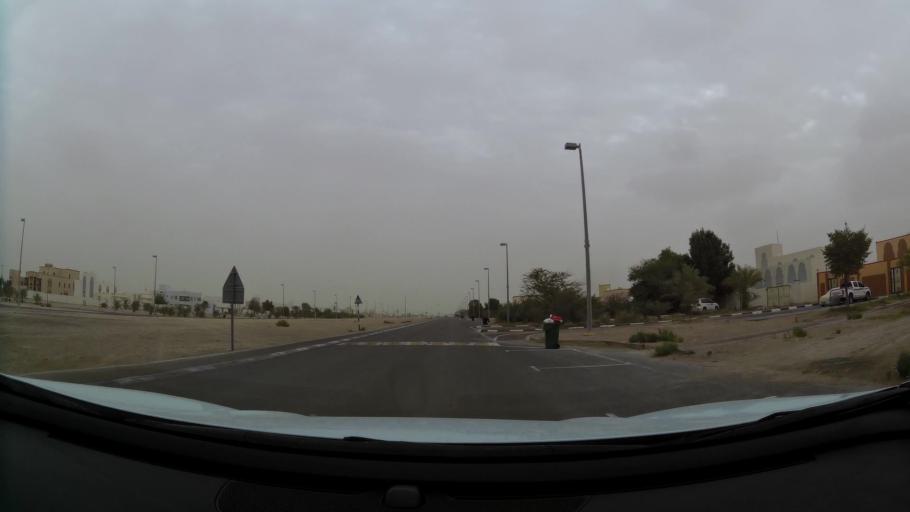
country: AE
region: Abu Dhabi
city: Abu Dhabi
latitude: 24.4238
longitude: 54.7327
